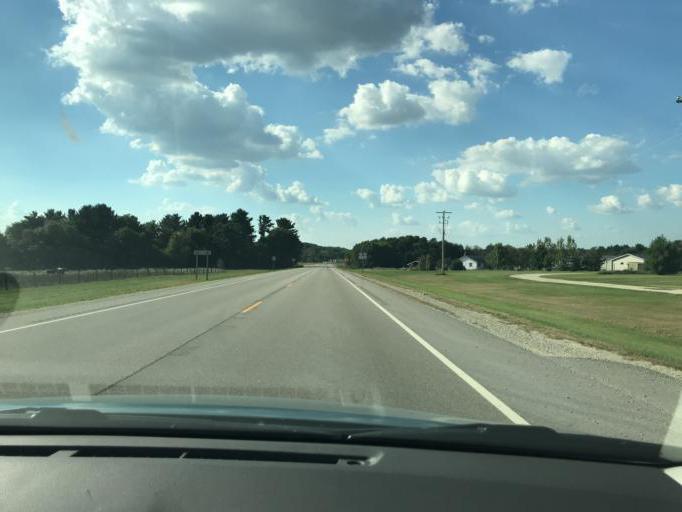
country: US
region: Wisconsin
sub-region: Green County
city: Brodhead
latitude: 42.5887
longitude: -89.3937
